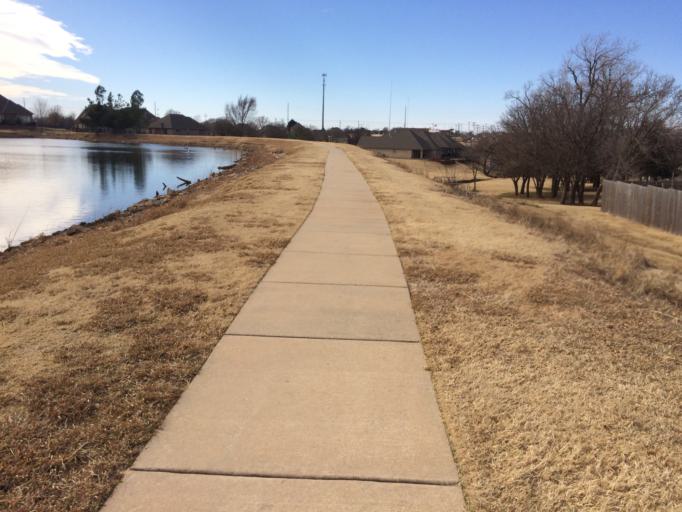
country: US
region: Oklahoma
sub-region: Cleveland County
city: Hall Park
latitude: 35.2178
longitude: -97.4011
